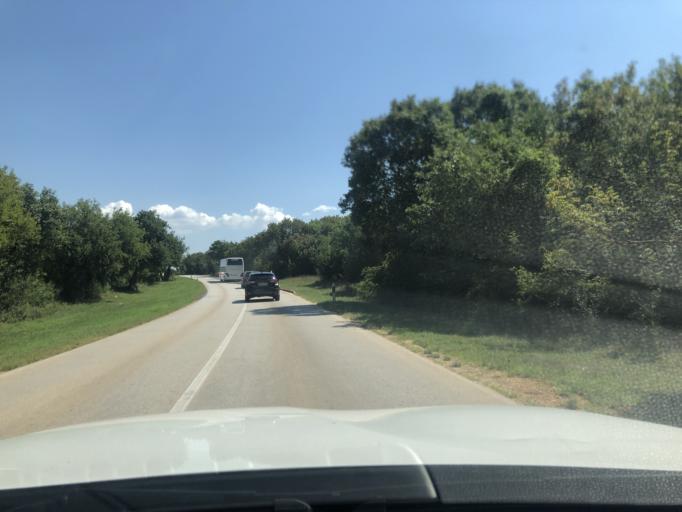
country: HR
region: Istarska
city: Vodnjan
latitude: 45.0369
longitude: 13.7837
